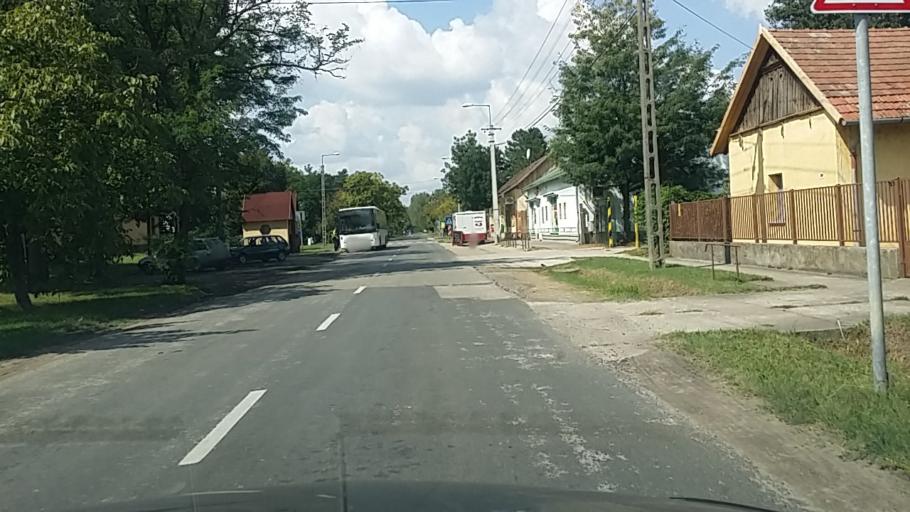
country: HU
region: Bacs-Kiskun
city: Tiszaalpar
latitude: 46.7524
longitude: 20.0355
